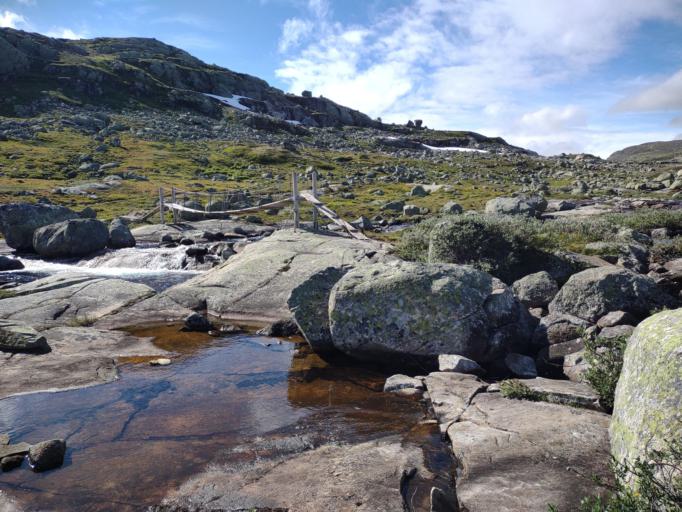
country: NO
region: Buskerud
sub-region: Hol
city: Geilo
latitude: 60.4805
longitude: 7.6836
